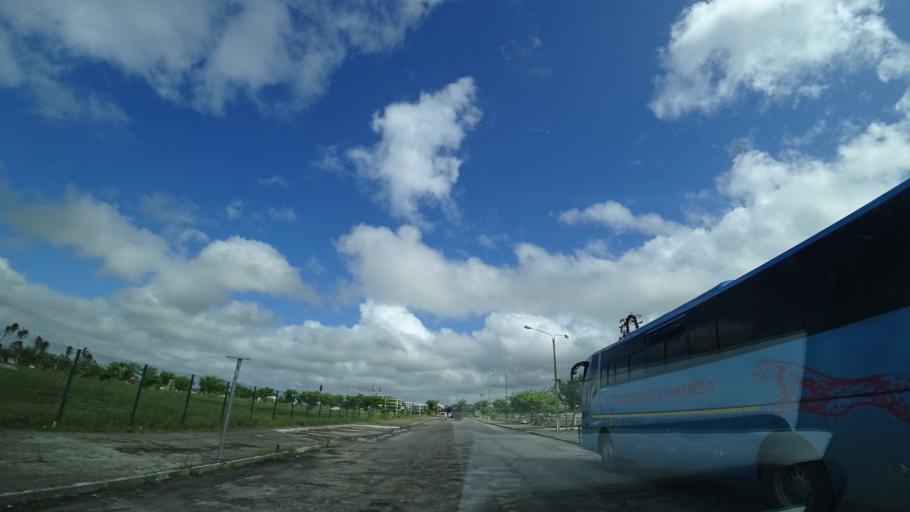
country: MZ
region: Sofala
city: Beira
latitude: -19.7997
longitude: 34.9020
